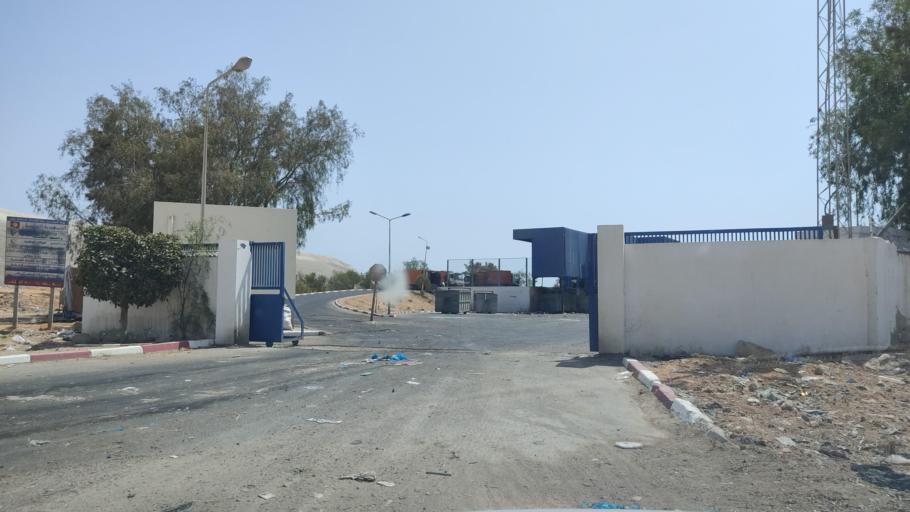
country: TN
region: Safaqis
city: Sfax
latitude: 34.6927
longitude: 10.7270
